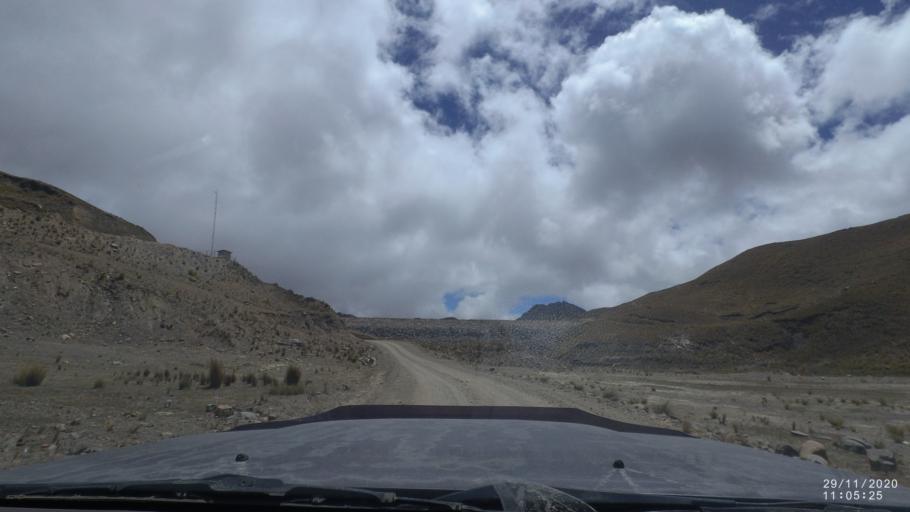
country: BO
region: Cochabamba
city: Cochabamba
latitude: -17.1869
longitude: -66.2111
